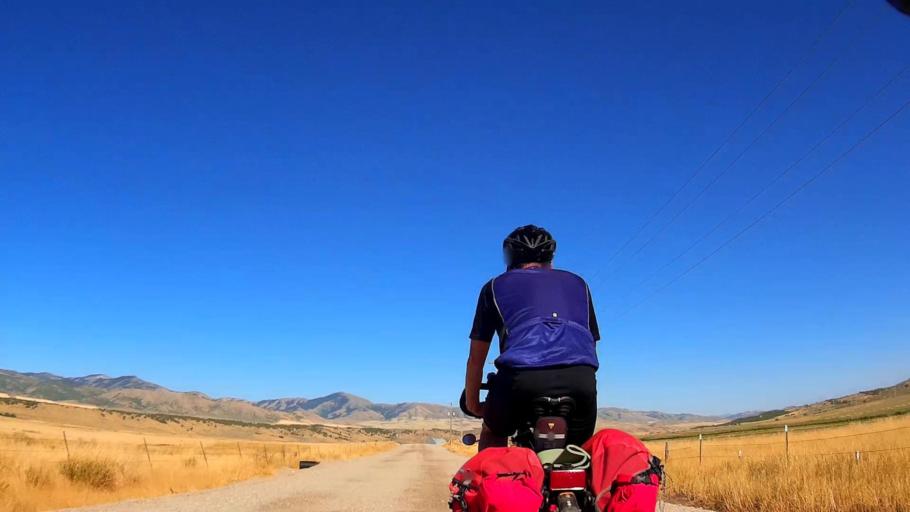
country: US
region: Idaho
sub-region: Oneida County
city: Malad City
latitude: 42.3978
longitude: -112.1244
